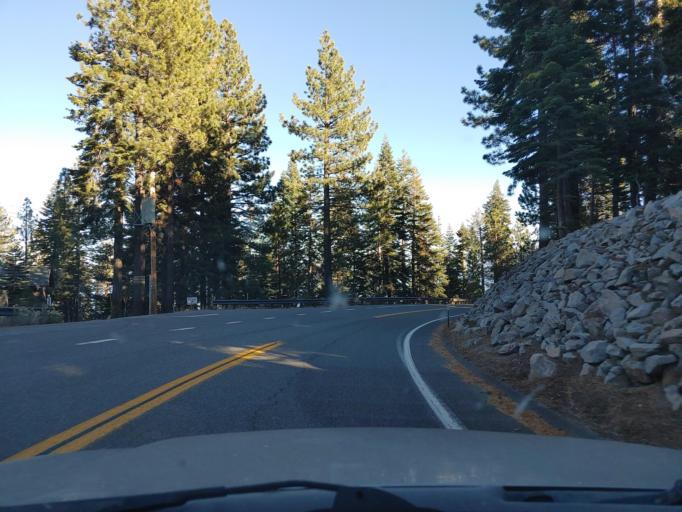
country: US
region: California
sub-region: Placer County
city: Tahoma
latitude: 39.0145
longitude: -120.1201
